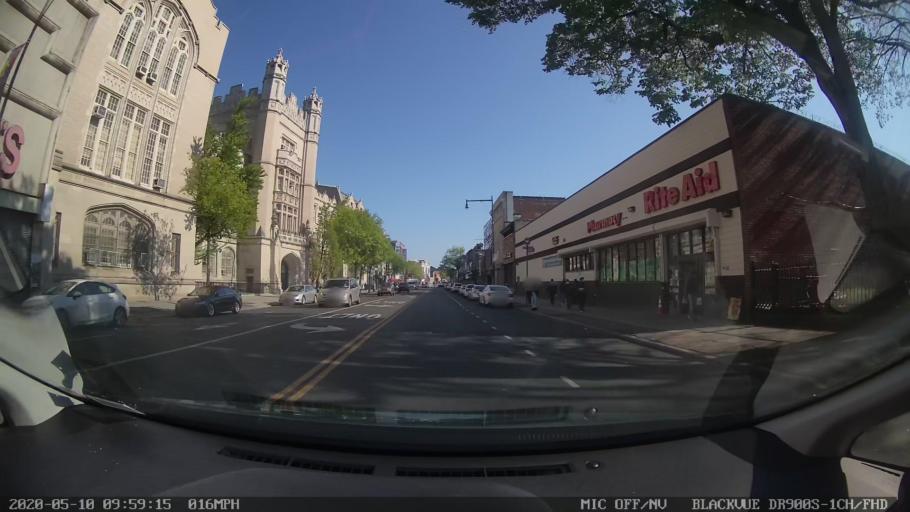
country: US
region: New York
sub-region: Kings County
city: Brooklyn
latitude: 40.6502
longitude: -73.9586
